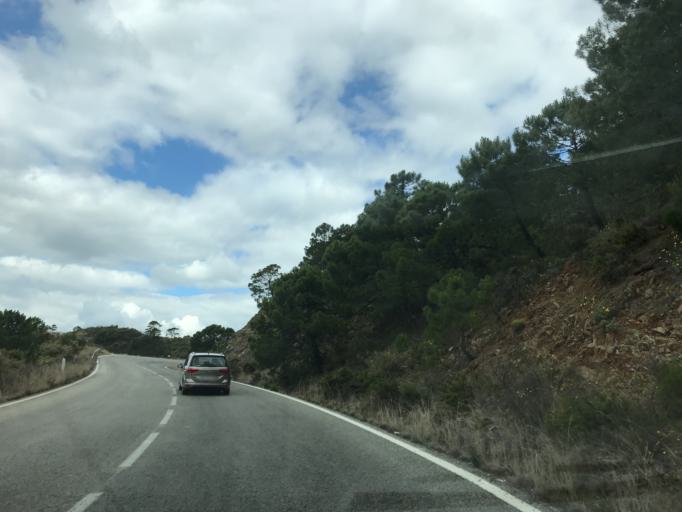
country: ES
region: Andalusia
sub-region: Provincia de Malaga
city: Benahavis
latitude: 36.5539
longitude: -5.0317
